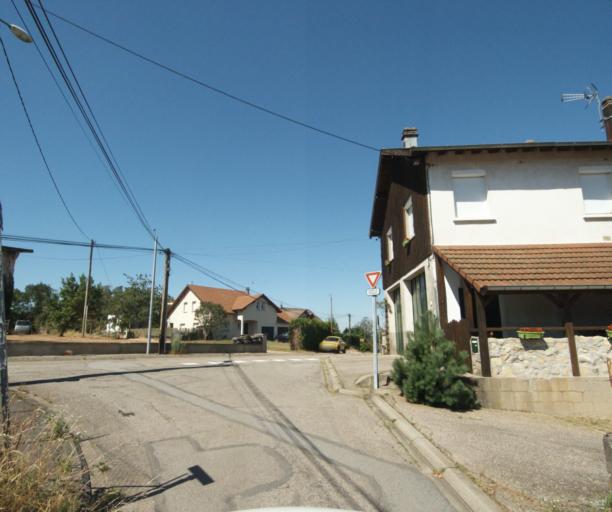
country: FR
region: Lorraine
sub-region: Departement des Vosges
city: Epinal
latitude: 48.1787
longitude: 6.4787
